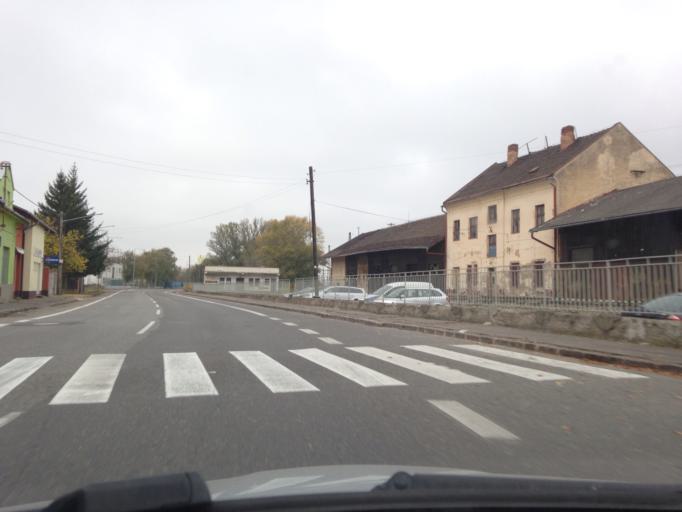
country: SK
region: Nitriansky
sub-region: Okres Nove Zamky
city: Sturovo
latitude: 47.7991
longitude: 18.6784
